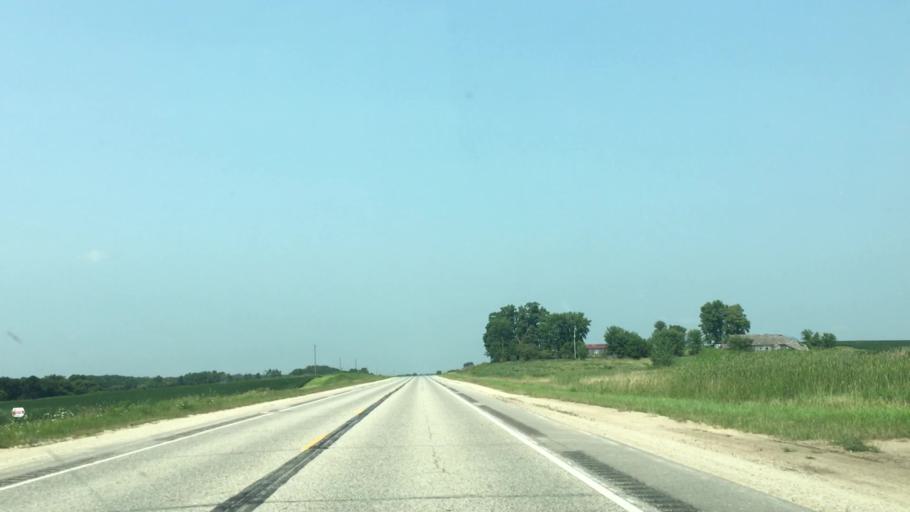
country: US
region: Iowa
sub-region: Fayette County
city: Fayette
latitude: 42.7936
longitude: -91.8050
